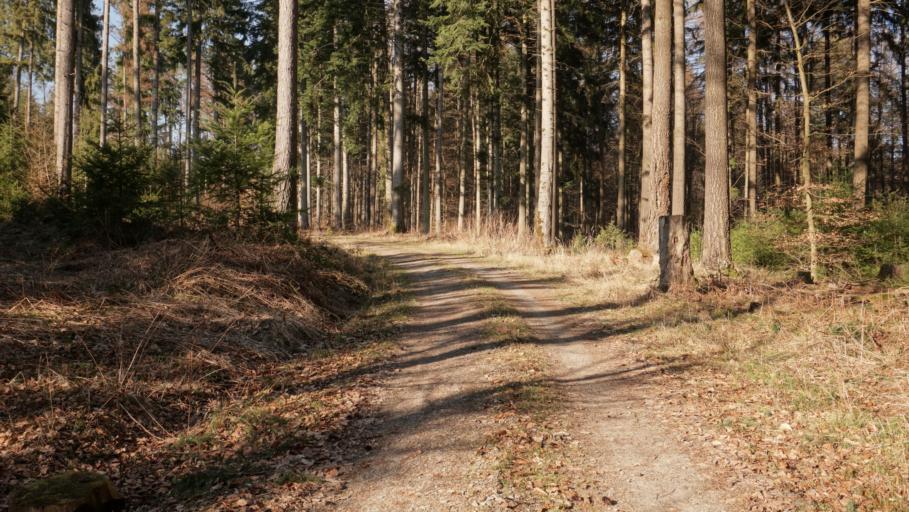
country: DE
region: Baden-Wuerttemberg
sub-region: Karlsruhe Region
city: Fahrenbach
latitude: 49.4453
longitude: 9.1472
